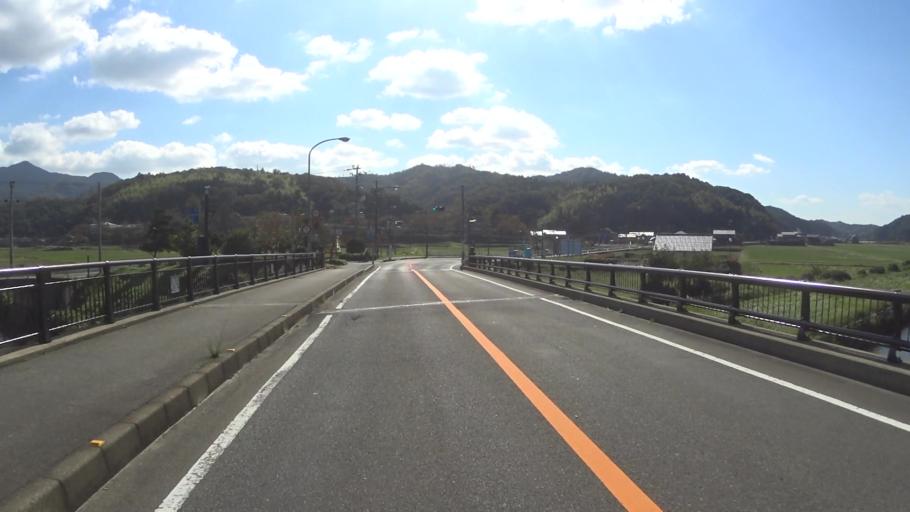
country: JP
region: Kyoto
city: Miyazu
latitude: 35.7142
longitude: 135.1055
